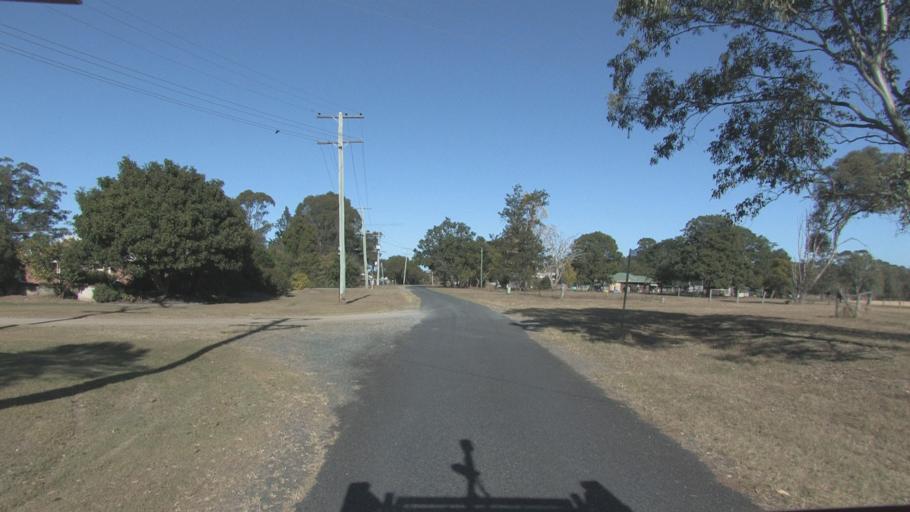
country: AU
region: Queensland
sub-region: Logan
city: Chambers Flat
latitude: -27.7605
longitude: 153.0519
